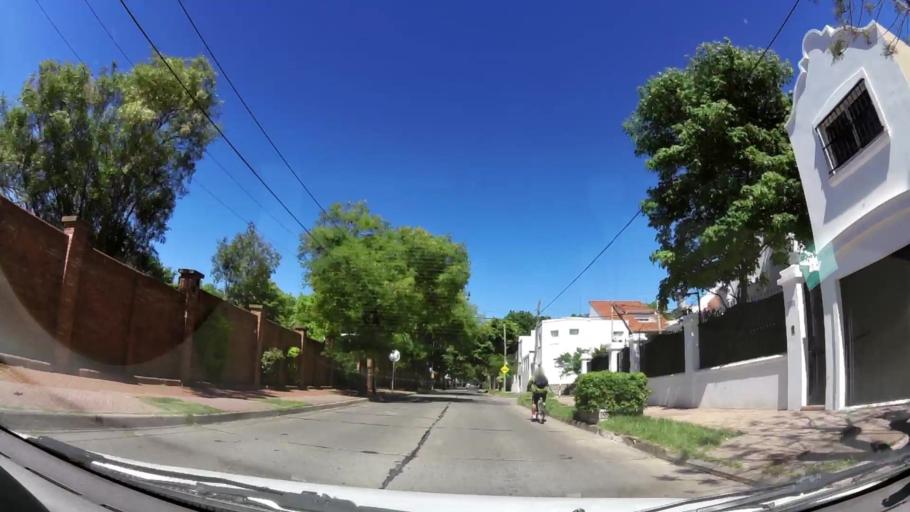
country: AR
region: Buenos Aires
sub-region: Partido de Vicente Lopez
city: Olivos
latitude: -34.5150
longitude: -58.4861
